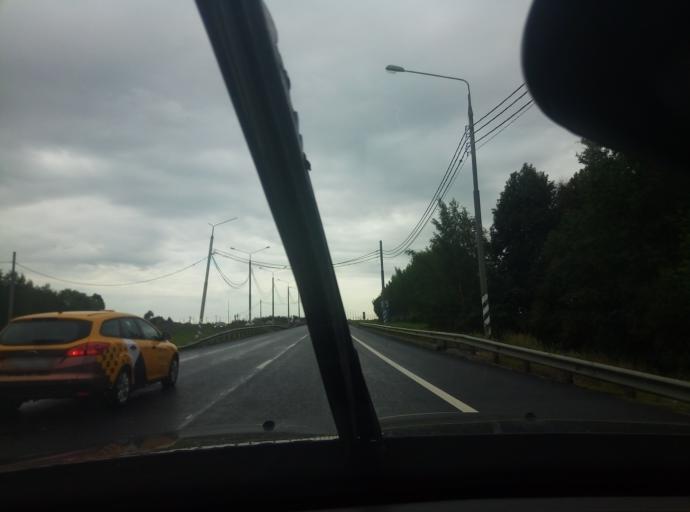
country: RU
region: Tula
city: Zaokskiy
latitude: 54.8118
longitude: 37.4813
